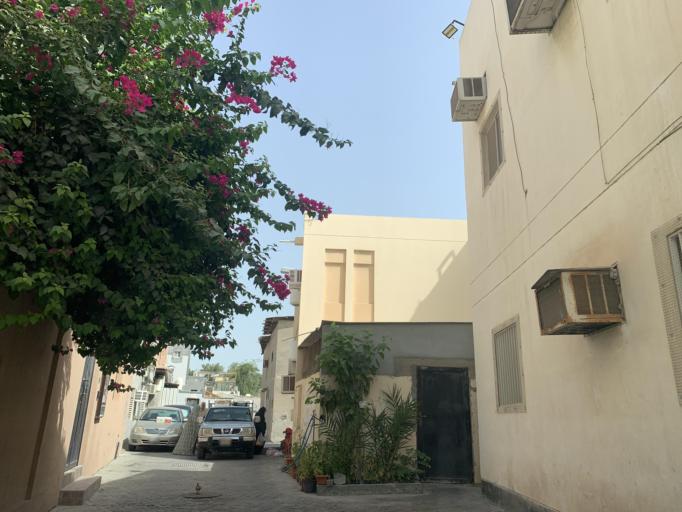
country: BH
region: Northern
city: Sitrah
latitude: 26.1340
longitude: 50.5968
